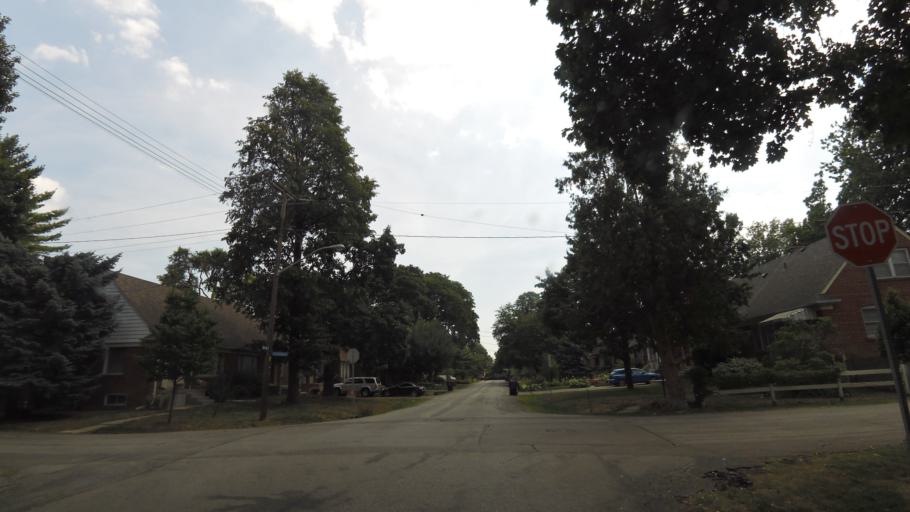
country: CA
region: Ontario
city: Etobicoke
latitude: 43.6426
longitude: -79.5250
